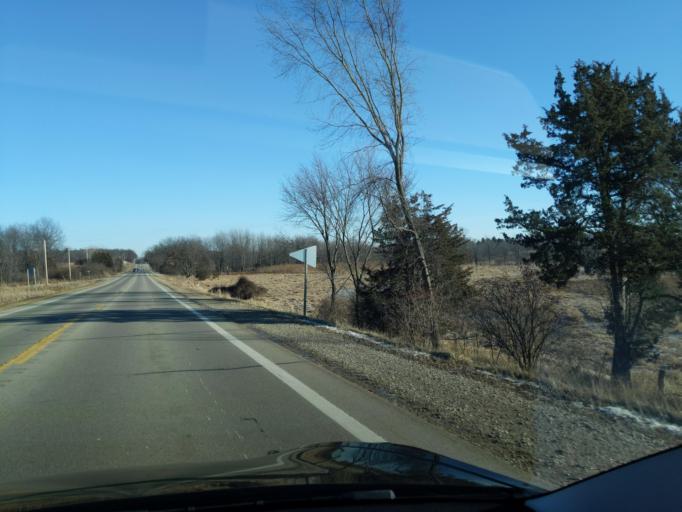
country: US
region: Michigan
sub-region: Ingham County
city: Leslie
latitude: 42.3947
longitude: -84.3069
